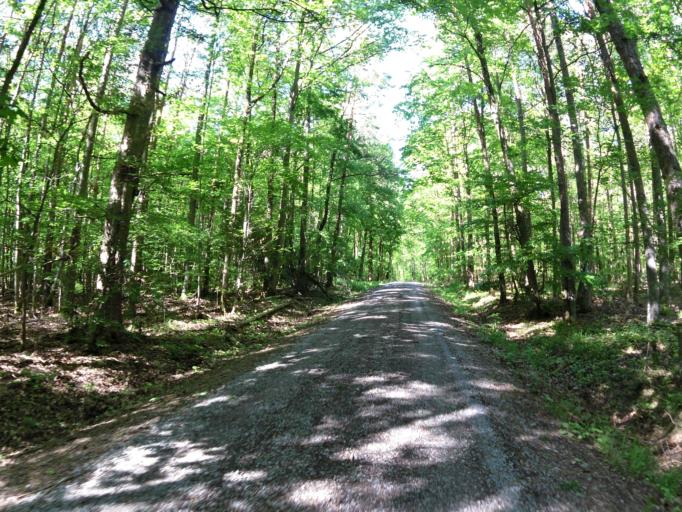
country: DE
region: Bavaria
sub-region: Regierungsbezirk Unterfranken
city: Wuerzburg
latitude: 49.7391
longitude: 9.8851
